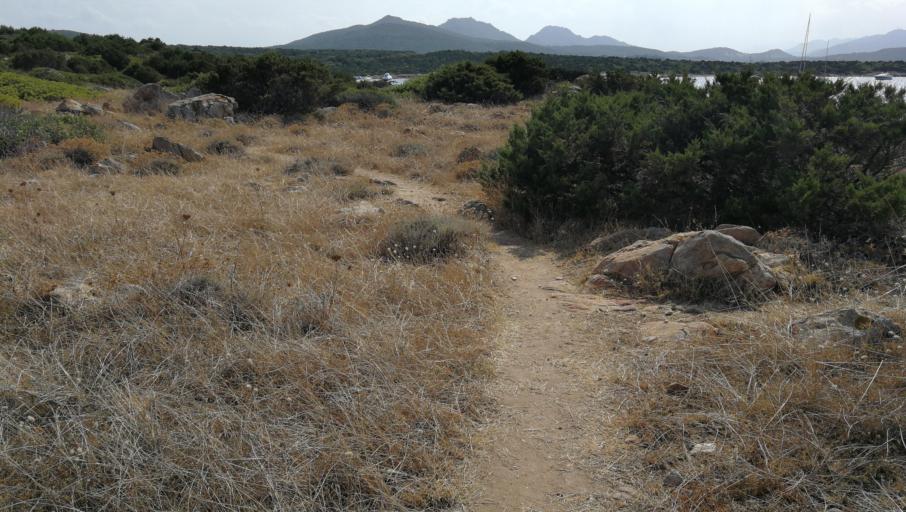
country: IT
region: Sardinia
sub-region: Provincia di Olbia-Tempio
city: Golfo Aranci
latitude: 41.0146
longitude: 9.5876
